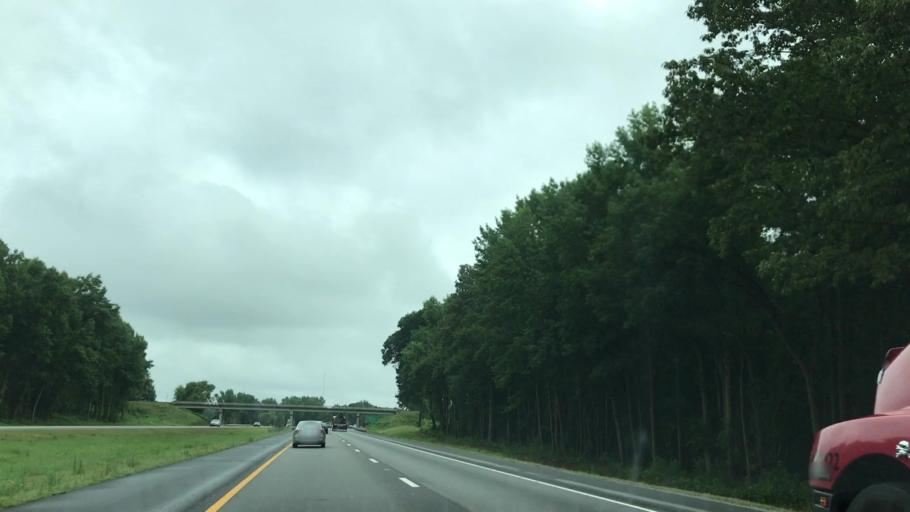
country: US
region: North Carolina
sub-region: Halifax County
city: Enfield
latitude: 36.1542
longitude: -77.7835
